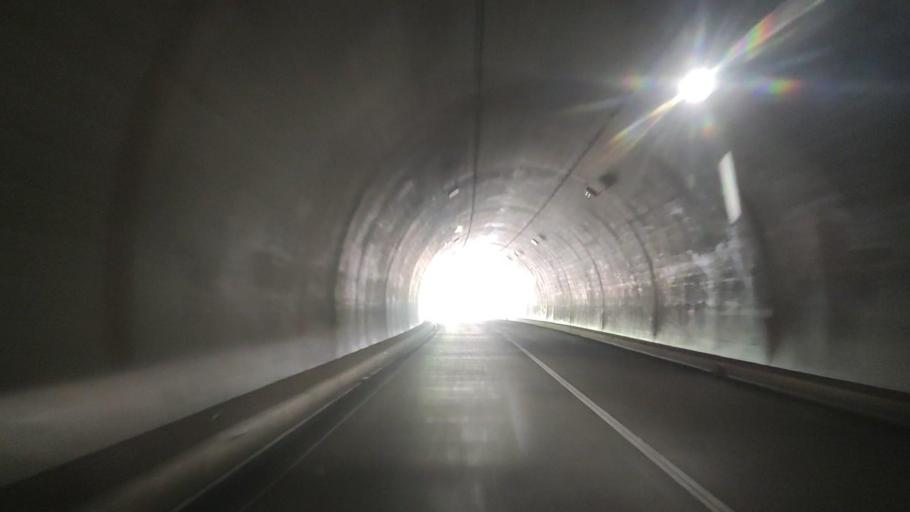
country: JP
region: Fukui
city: Ono
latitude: 35.8326
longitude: 136.4443
